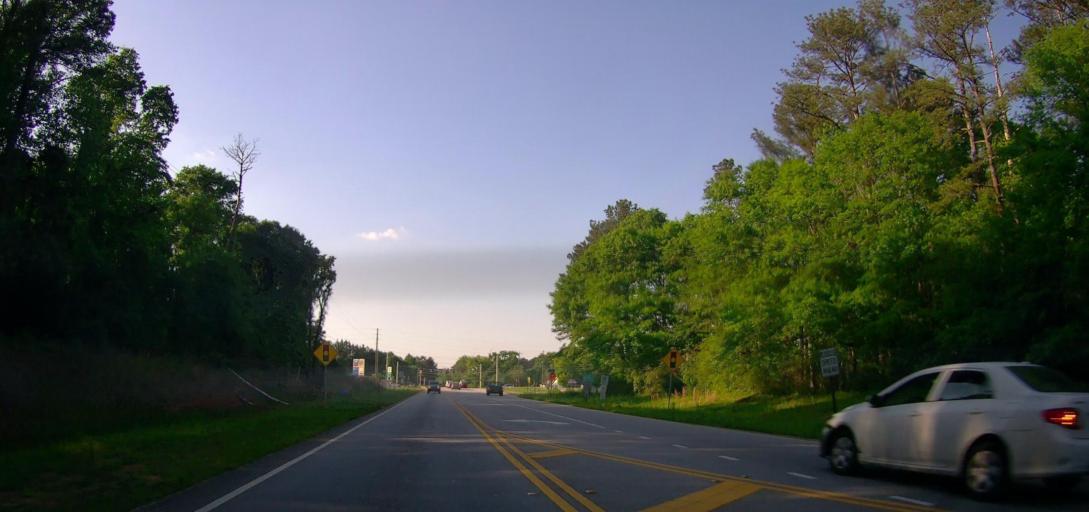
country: US
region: Georgia
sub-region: Newton County
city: Porterdale
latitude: 33.5638
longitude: -83.9018
